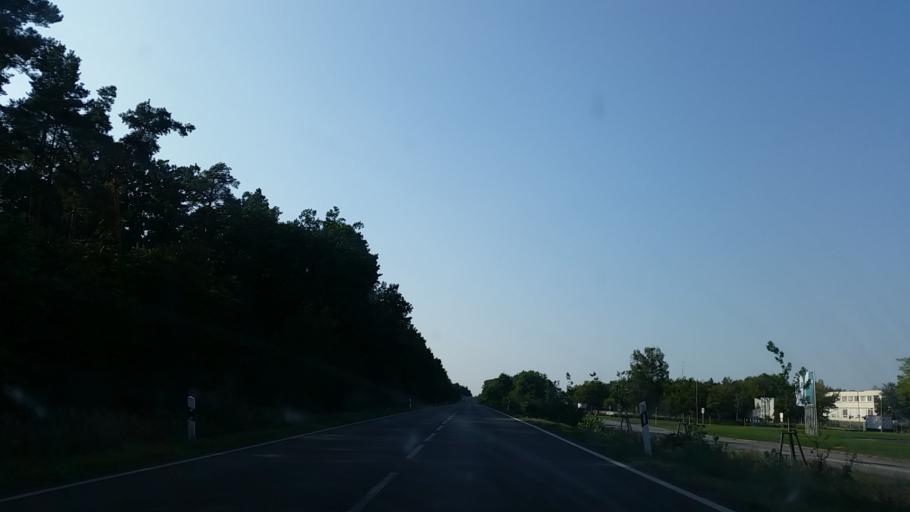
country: DE
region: Brandenburg
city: Meyenburg
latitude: 53.0876
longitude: 14.2264
